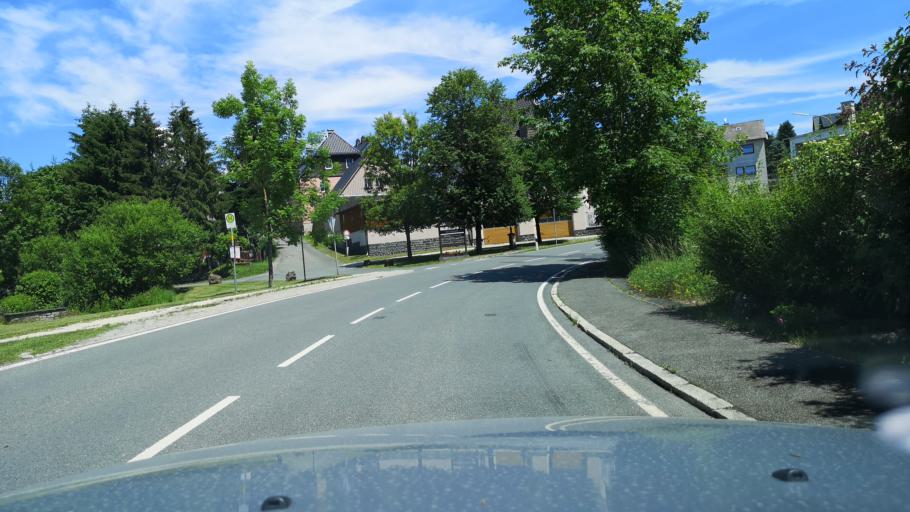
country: DE
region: Bavaria
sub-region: Upper Franconia
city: Teuschnitz
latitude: 50.3927
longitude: 11.3788
